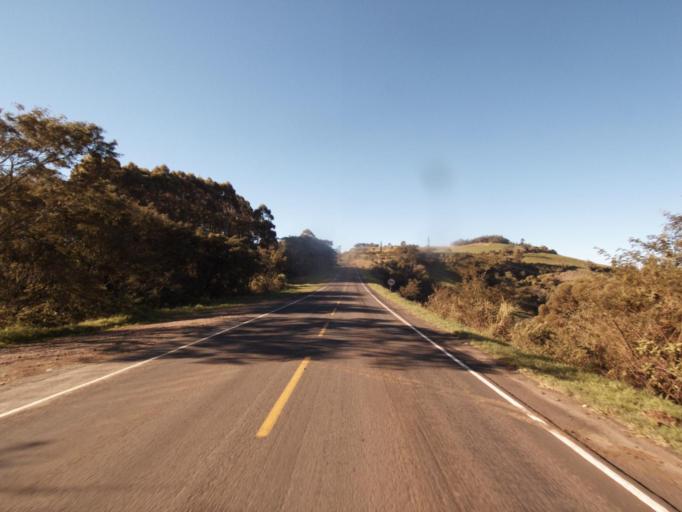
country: AR
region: Misiones
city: Bernardo de Irigoyen
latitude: -26.5030
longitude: -53.5094
